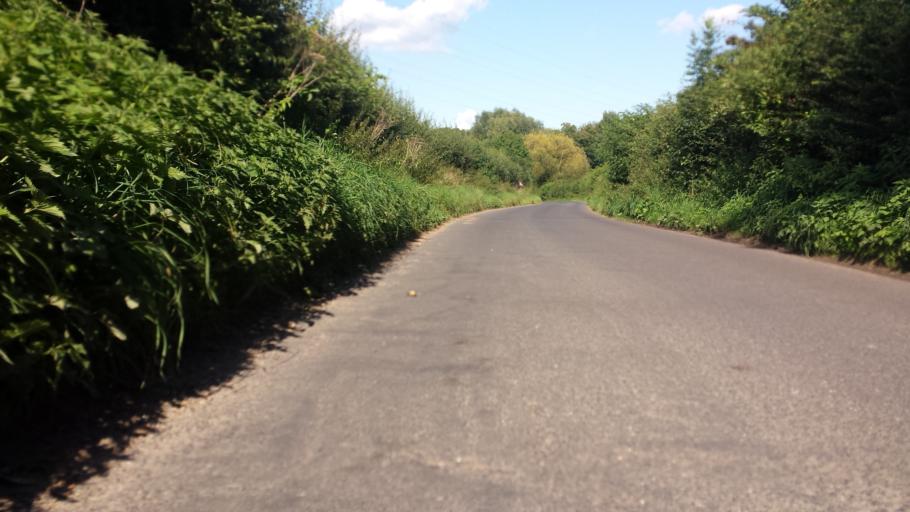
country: GB
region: England
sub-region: Kent
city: Shoreham
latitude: 51.3512
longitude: 0.1887
